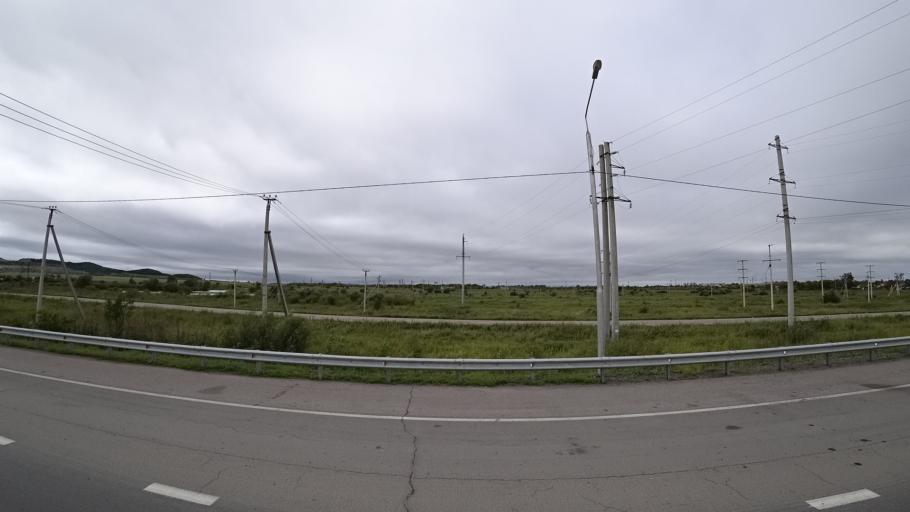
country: RU
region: Primorskiy
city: Monastyrishche
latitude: 44.1861
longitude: 132.4415
